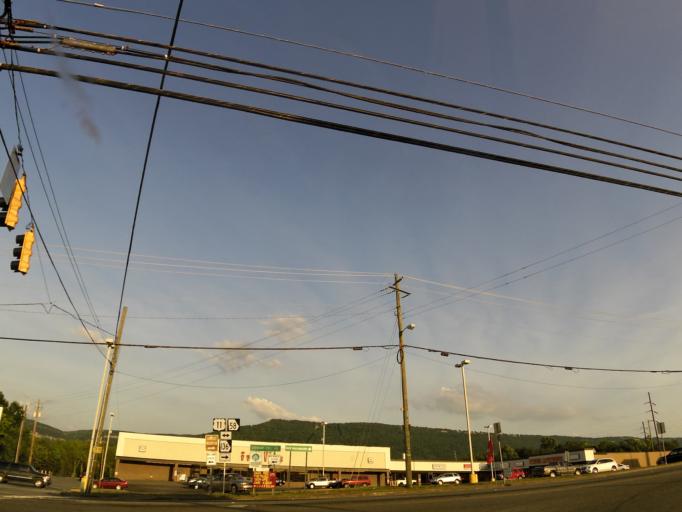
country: US
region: Georgia
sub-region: Dade County
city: Trenton
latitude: 34.8687
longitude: -85.5120
